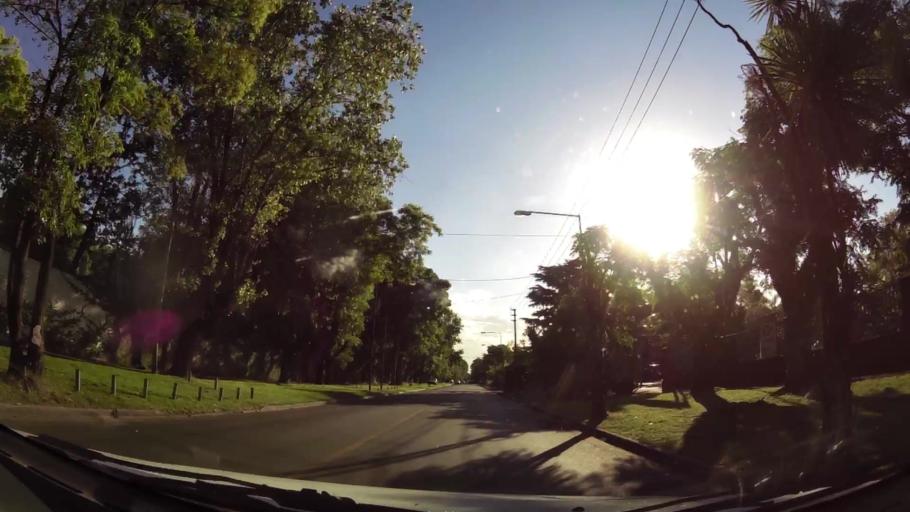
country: AR
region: Buenos Aires
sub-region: Partido de San Isidro
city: San Isidro
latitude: -34.4811
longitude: -58.5369
